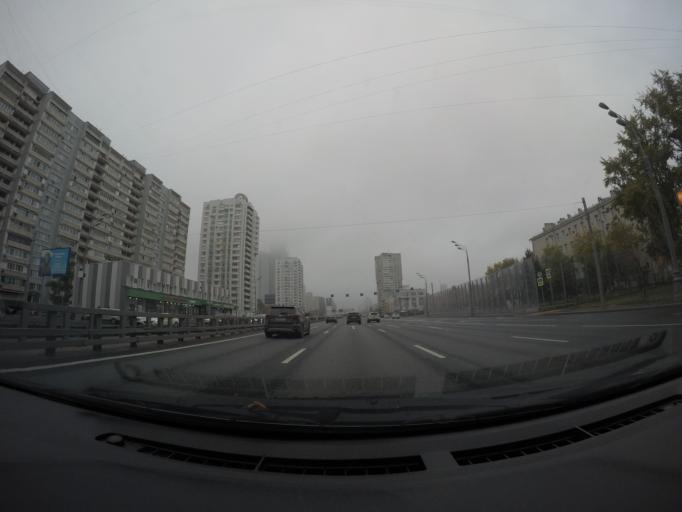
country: RU
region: Moskovskaya
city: Khoroshevo-Mnevniki
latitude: 55.7735
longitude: 37.4863
